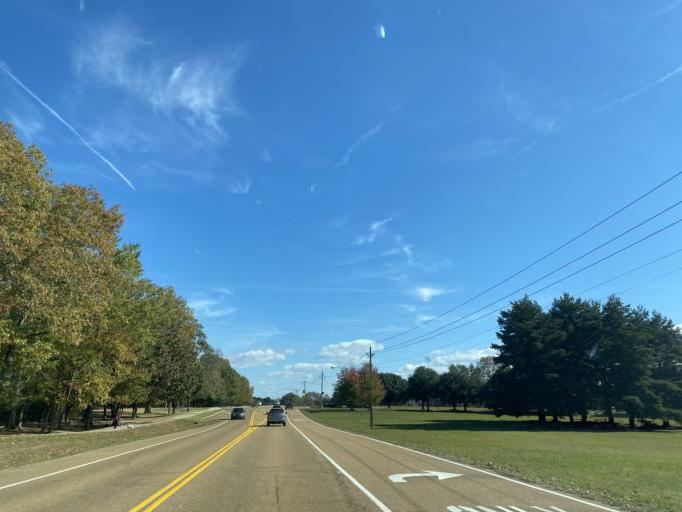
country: US
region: Mississippi
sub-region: Madison County
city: Madison
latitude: 32.4575
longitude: -90.0963
